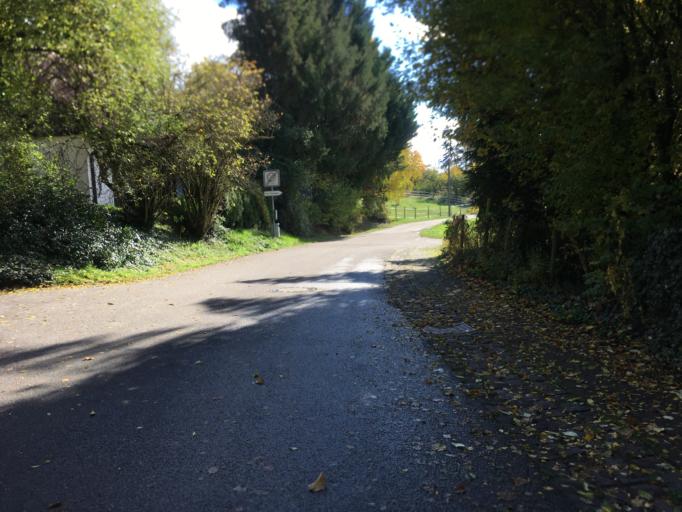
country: DE
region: Baden-Wuerttemberg
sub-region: Regierungsbezirk Stuttgart
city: Pfedelbach
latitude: 49.1783
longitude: 9.4884
